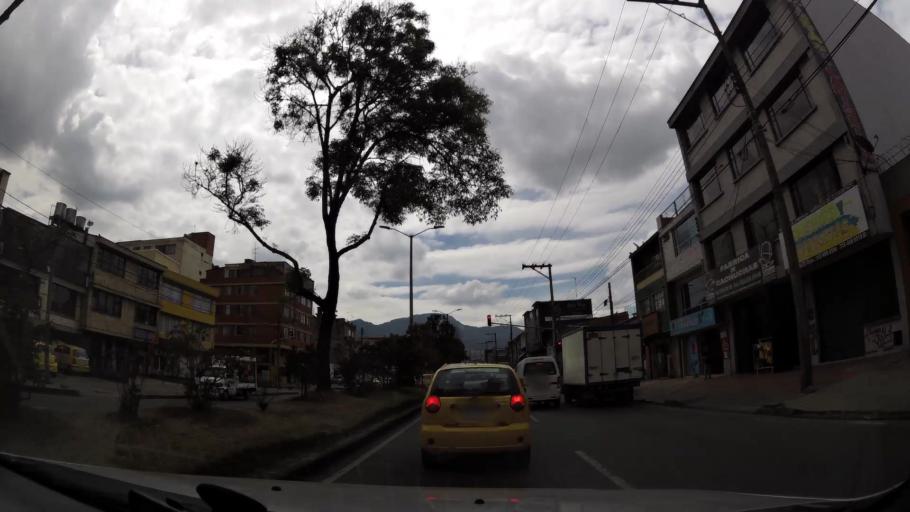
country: CO
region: Bogota D.C.
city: Bogota
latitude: 4.6054
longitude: -74.1038
